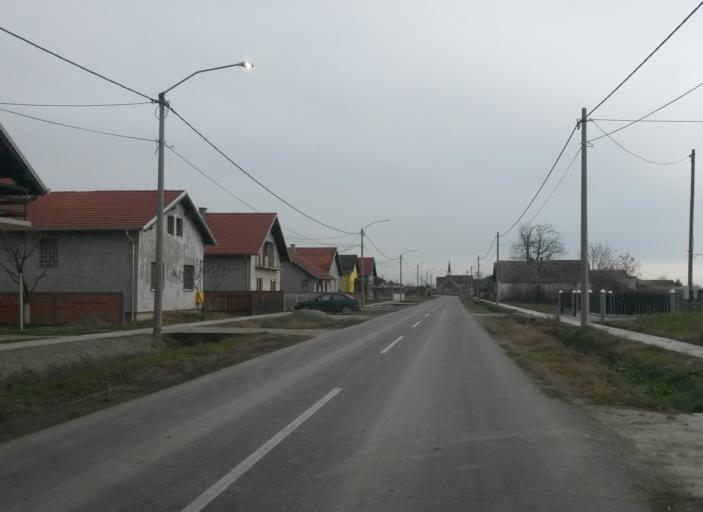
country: HR
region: Osjecko-Baranjska
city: Antunovac
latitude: 45.4897
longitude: 18.6291
